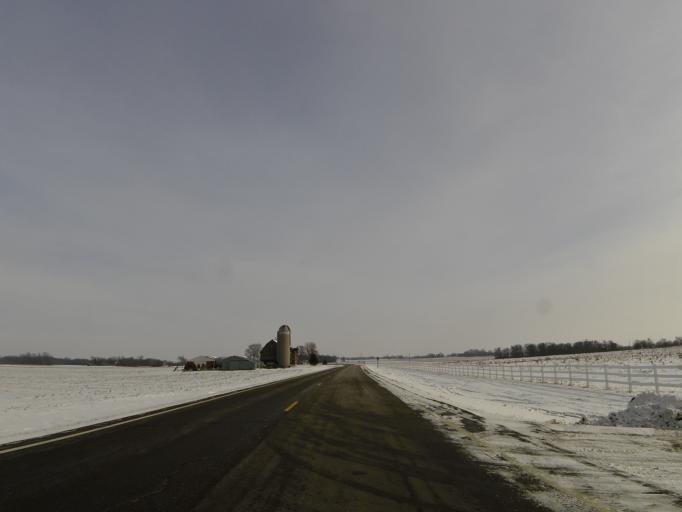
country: US
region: Minnesota
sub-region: McLeod County
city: Lester Prairie
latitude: 44.8767
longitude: -93.9757
